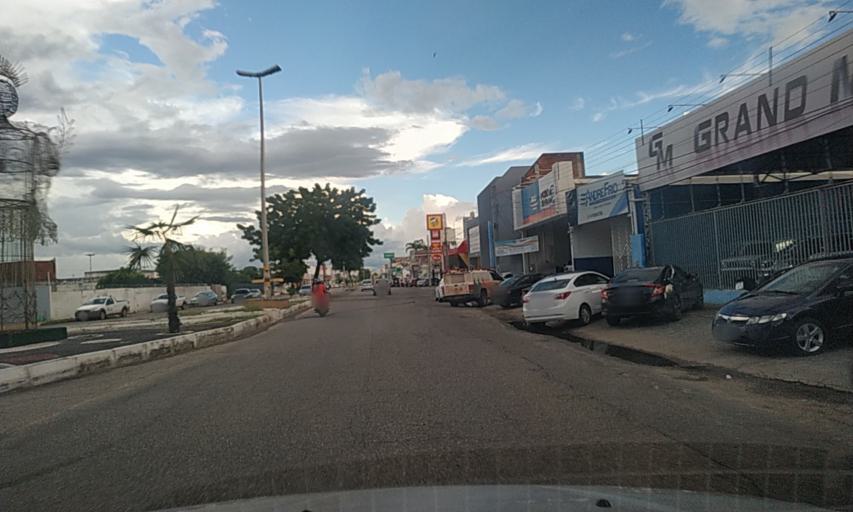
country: BR
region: Rio Grande do Norte
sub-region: Mossoro
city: Mossoro
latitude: -5.1965
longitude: -37.3414
